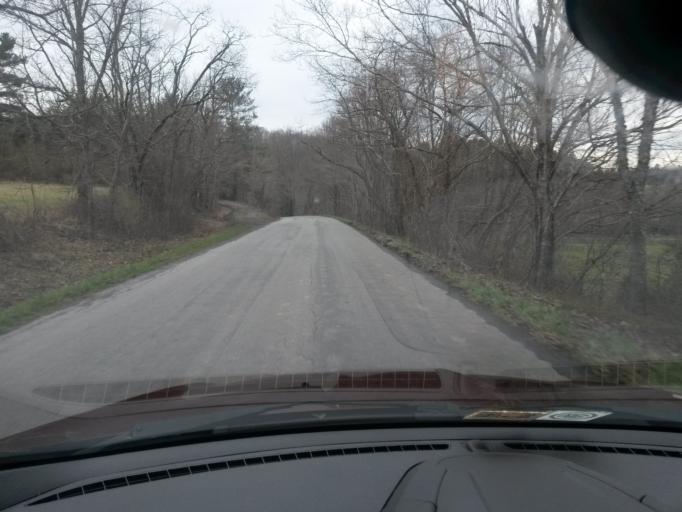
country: US
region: Virginia
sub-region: Bath County
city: Warm Springs
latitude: 38.0476
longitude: -79.8642
